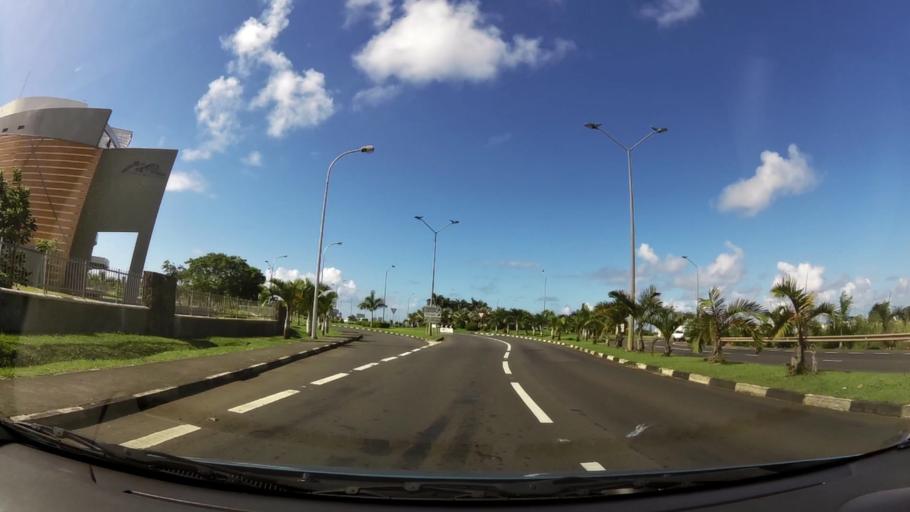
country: MU
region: Grand Port
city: Plaine Magnien
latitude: -20.4339
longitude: 57.6734
